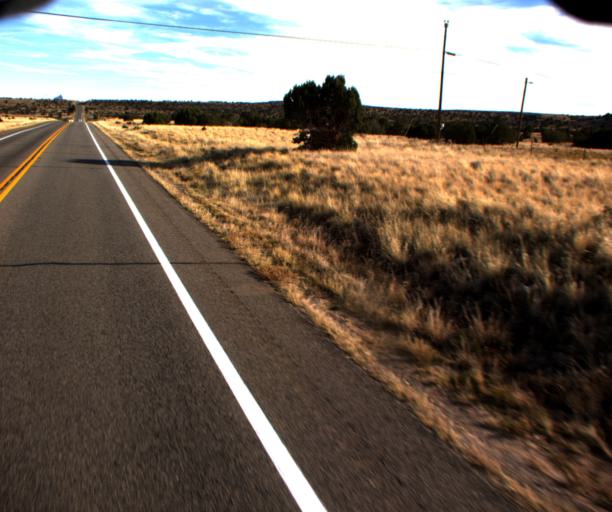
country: US
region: New Mexico
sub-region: San Juan County
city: Shiprock
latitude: 36.8903
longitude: -109.0596
